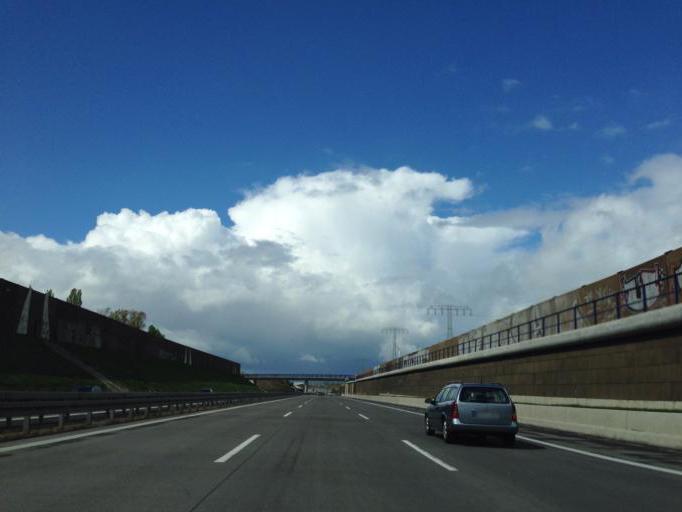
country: DE
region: Saxony
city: Taucha
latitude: 51.3807
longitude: 12.4521
